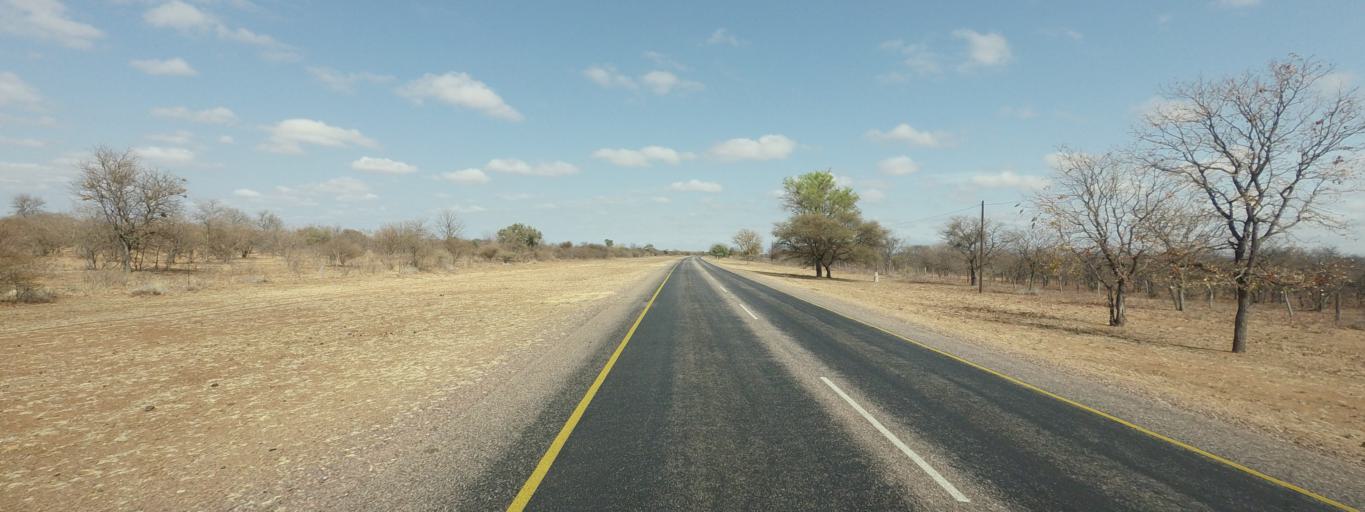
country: BW
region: Central
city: Ramokgonami
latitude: -22.7989
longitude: 27.4795
